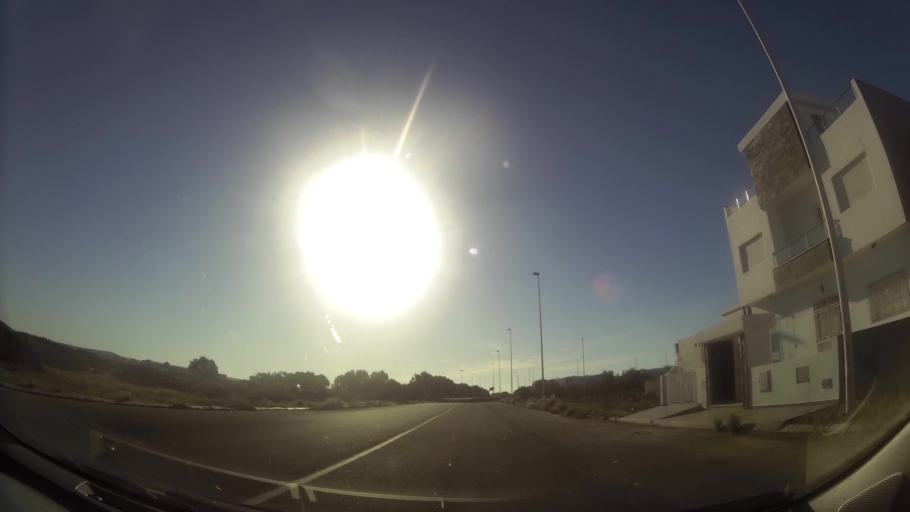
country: MA
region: Oriental
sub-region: Berkane-Taourirt
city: Madagh
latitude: 35.0908
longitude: -2.2602
